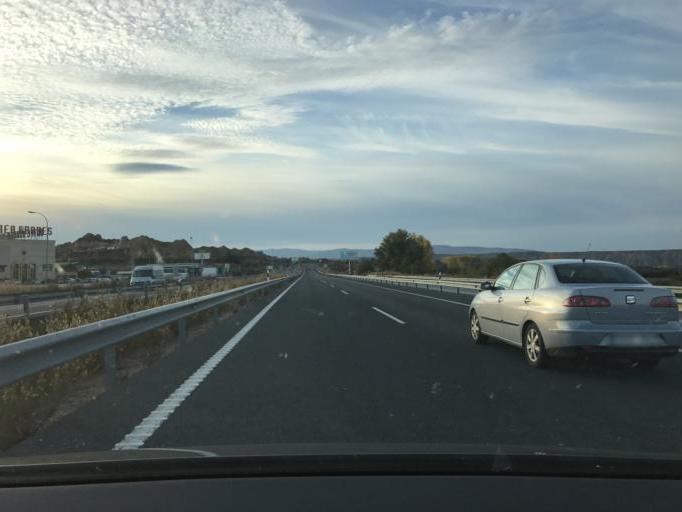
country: ES
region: Andalusia
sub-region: Provincia de Granada
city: Guadix
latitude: 37.3204
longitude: -3.1553
